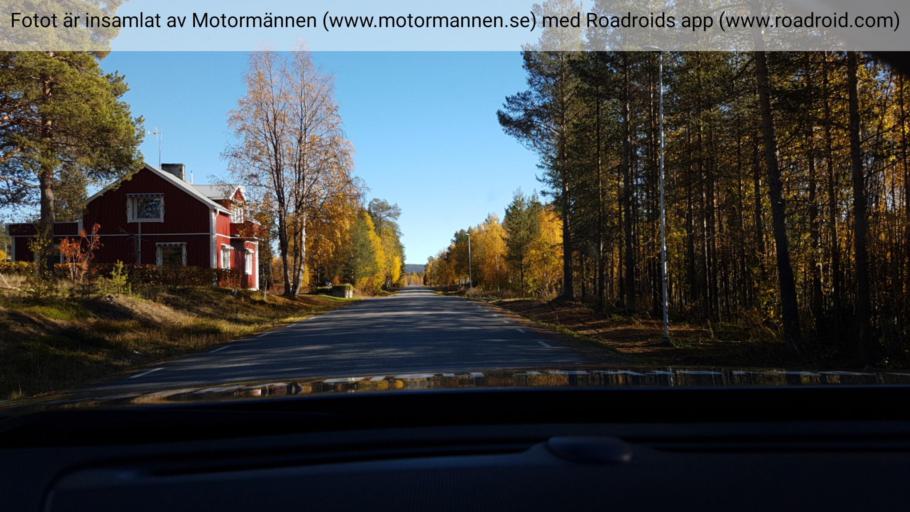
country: SE
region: Norrbotten
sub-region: Gallivare Kommun
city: Gaellivare
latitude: 66.7553
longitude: 20.9594
